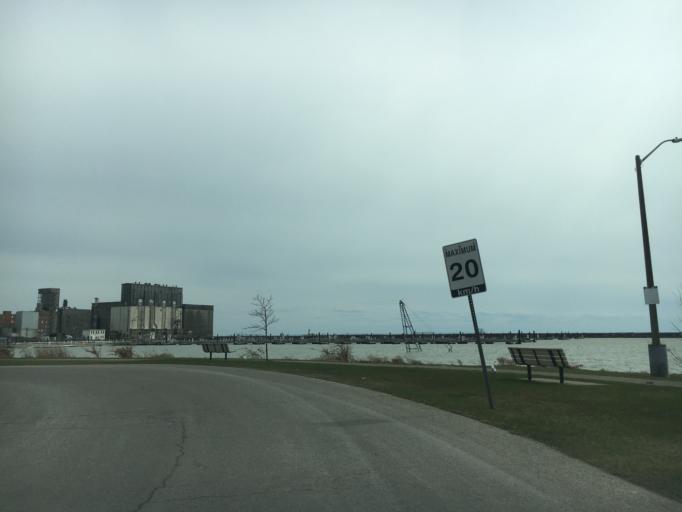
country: CA
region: Ontario
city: Port Colborne
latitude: 42.8783
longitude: -79.2570
